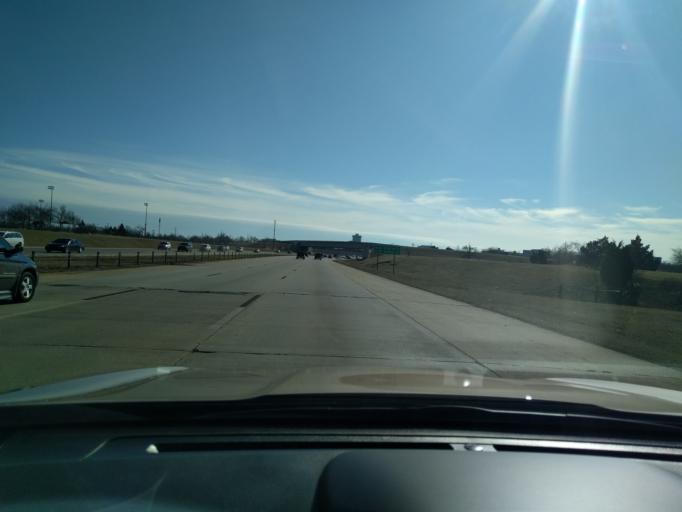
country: US
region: Oklahoma
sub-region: Oklahoma County
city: Nichols Hills
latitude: 35.5473
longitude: -97.5763
